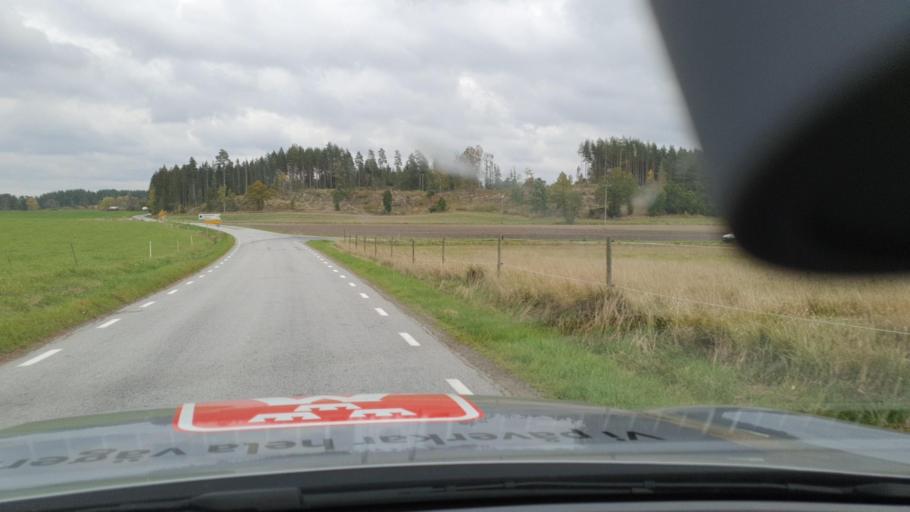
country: SE
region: OEstergoetland
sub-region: Soderkopings Kommun
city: Soederkoeping
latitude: 58.4693
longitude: 16.2783
